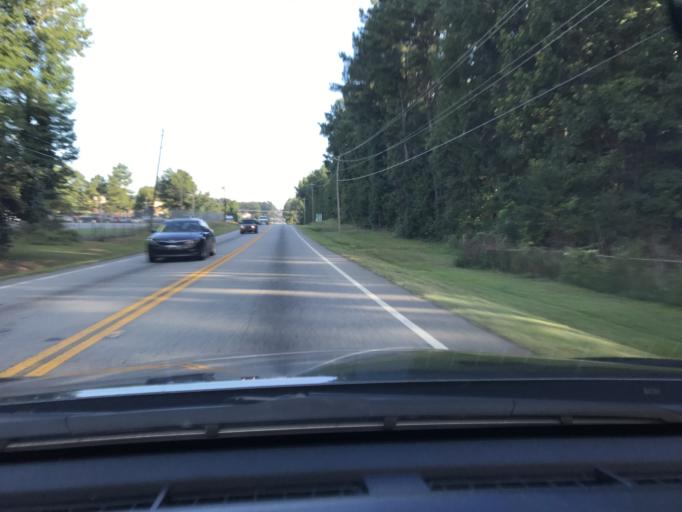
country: US
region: Georgia
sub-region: Clayton County
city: Lake City
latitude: 33.6039
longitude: -84.3006
